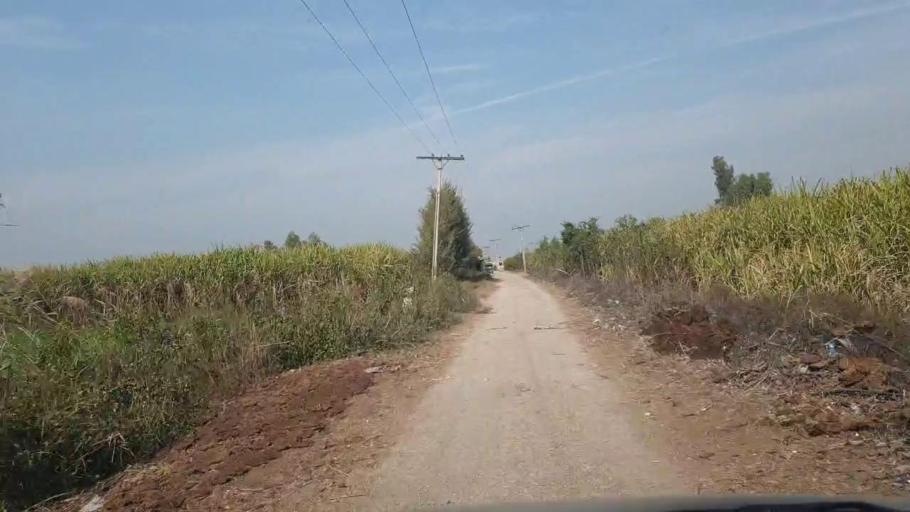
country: PK
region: Sindh
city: Shahdadpur
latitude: 25.8772
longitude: 68.5964
